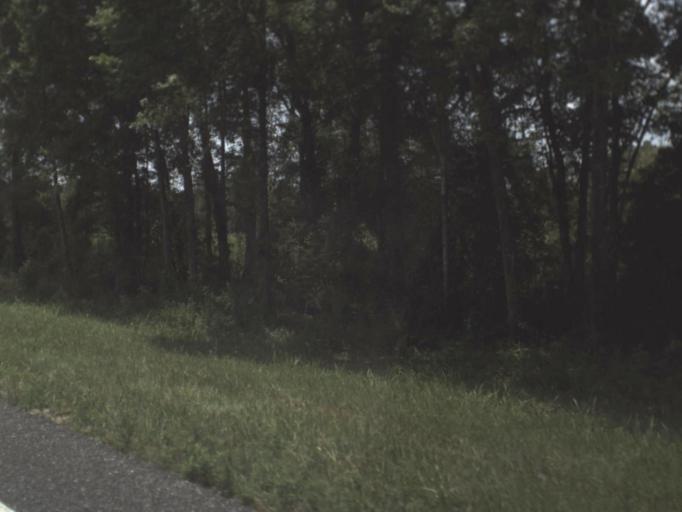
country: US
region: Florida
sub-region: Taylor County
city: Perry
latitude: 29.9503
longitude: -83.4566
